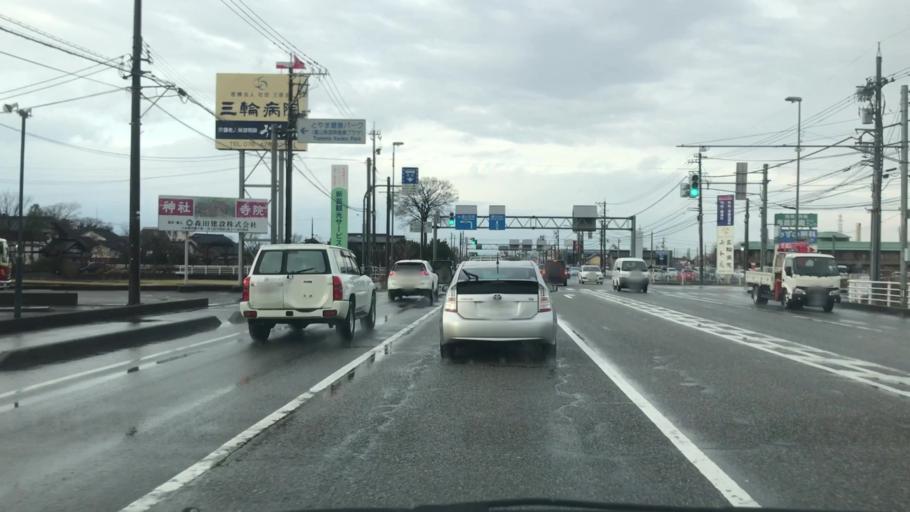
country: JP
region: Toyama
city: Toyama-shi
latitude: 36.6420
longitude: 137.2094
